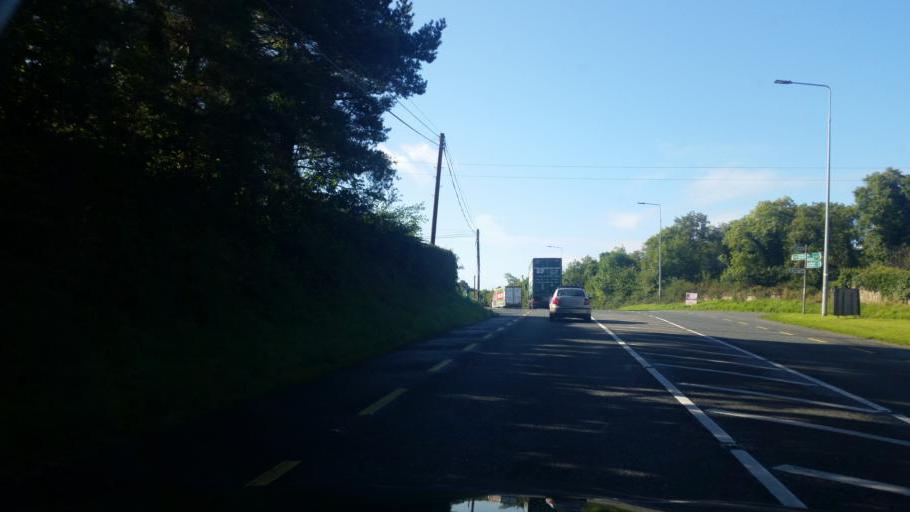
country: IE
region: Leinster
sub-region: An Iarmhi
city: Kilbeggan
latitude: 53.3311
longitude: -7.5119
